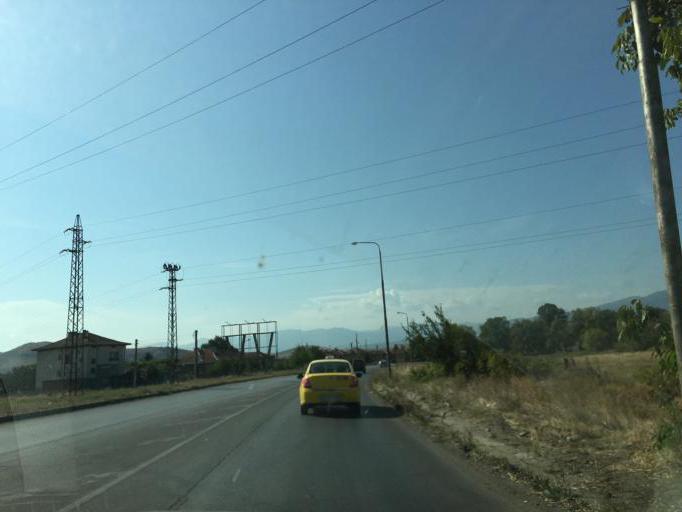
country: BG
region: Pazardzhik
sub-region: Obshtina Pazardzhik
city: Pazardzhik
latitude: 42.1645
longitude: 24.3157
